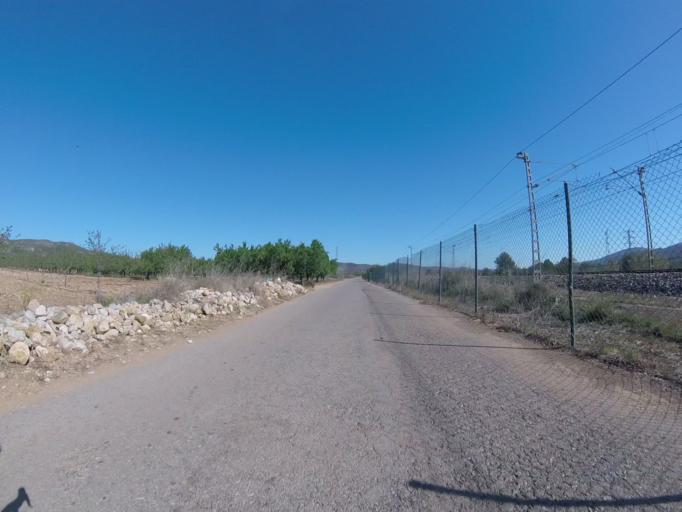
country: ES
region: Valencia
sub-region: Provincia de Castello
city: Alcala de Xivert
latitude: 40.3164
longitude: 0.2333
